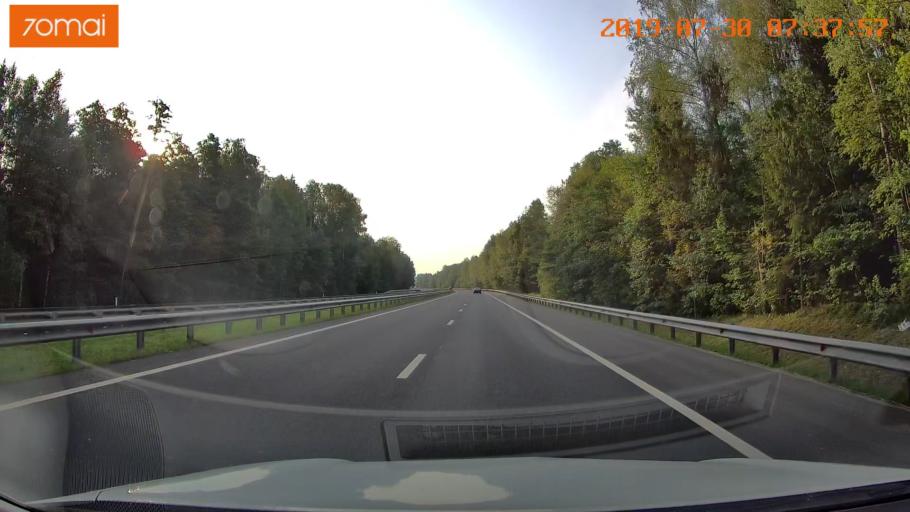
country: RU
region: Kaliningrad
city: Gvardeysk
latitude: 54.6524
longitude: 21.1558
